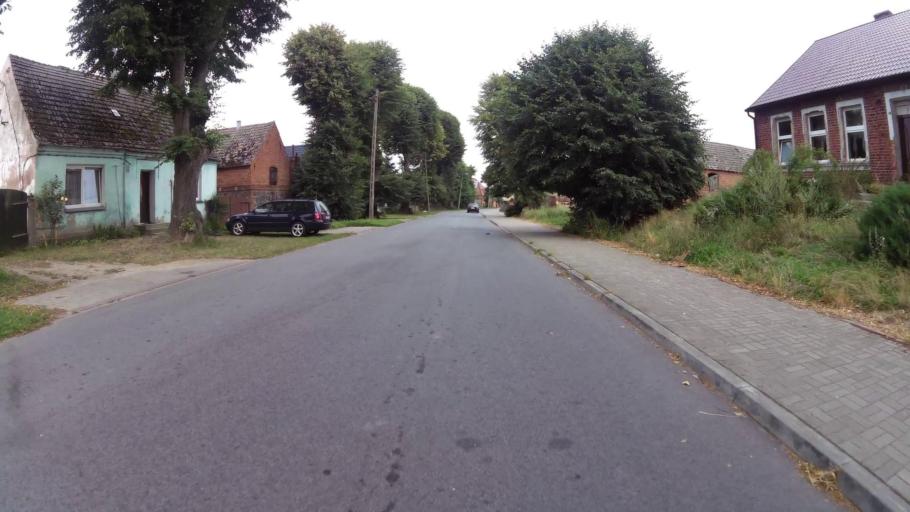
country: PL
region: West Pomeranian Voivodeship
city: Trzcinsko Zdroj
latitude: 52.9111
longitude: 14.6519
